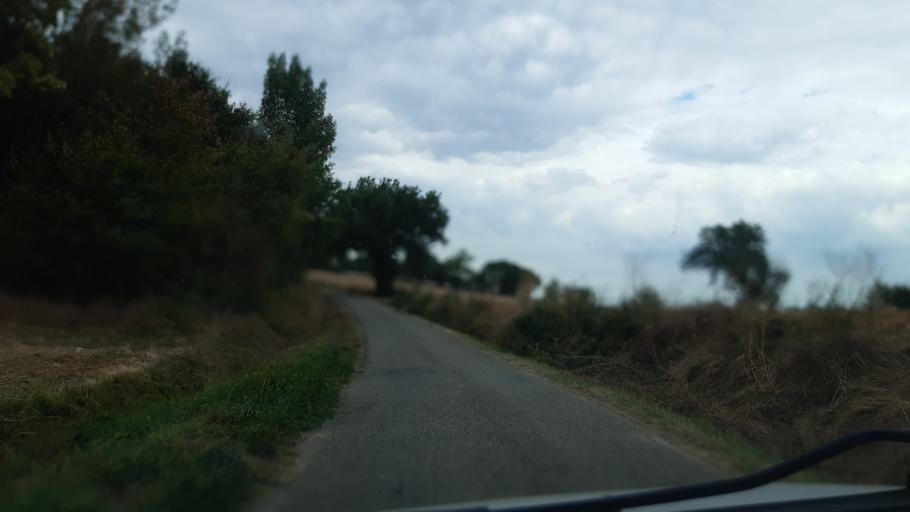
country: FR
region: Midi-Pyrenees
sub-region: Departement du Gers
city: Gimont
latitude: 43.6837
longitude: 0.9600
